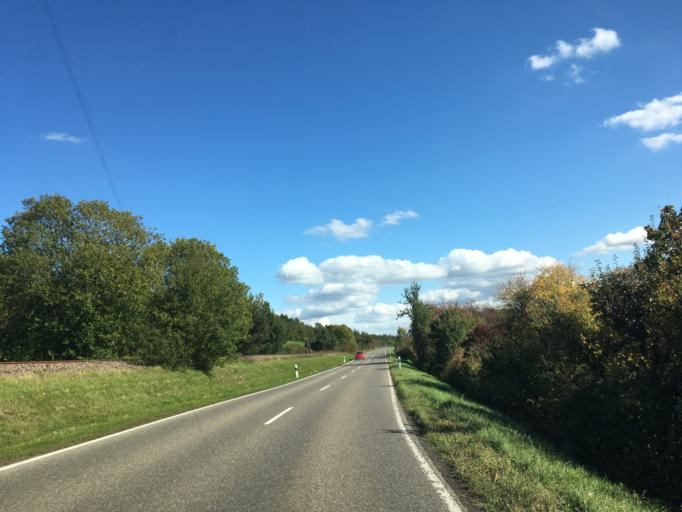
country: DE
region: Baden-Wuerttemberg
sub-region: Karlsruhe Region
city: Ostelsheim
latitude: 48.7271
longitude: 8.8640
